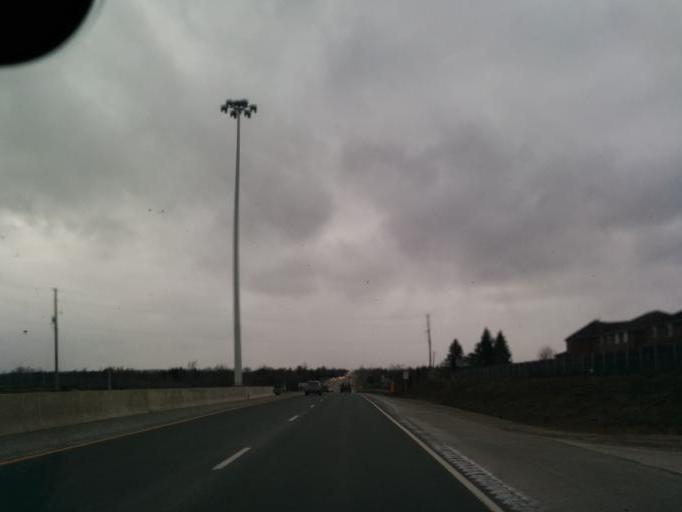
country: CA
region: Ontario
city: Brampton
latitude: 43.7431
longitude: -79.8374
